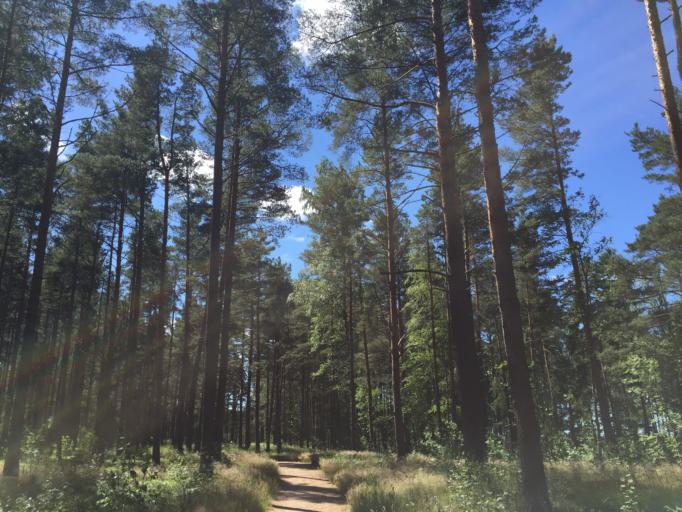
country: LV
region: Ventspils
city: Ventspils
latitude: 57.4397
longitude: 21.6568
